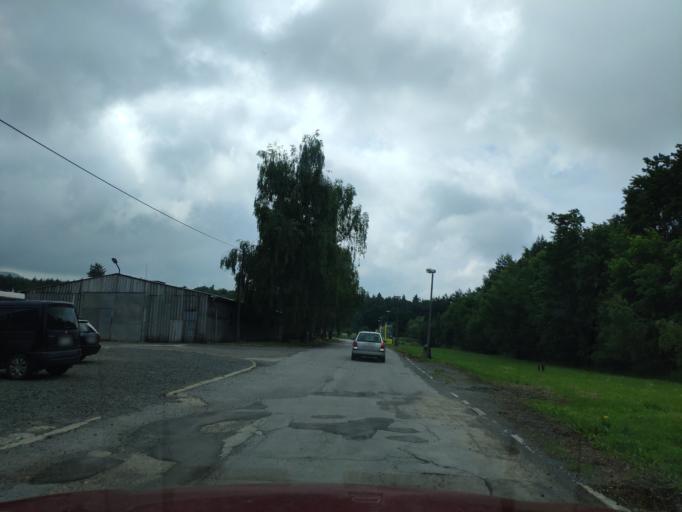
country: SK
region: Presovsky
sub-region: Okres Presov
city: Presov
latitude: 48.9991
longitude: 21.3193
